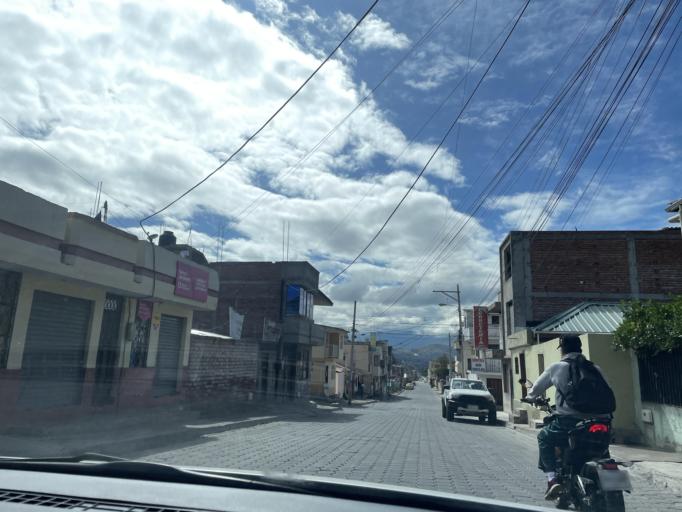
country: EC
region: Chimborazo
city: Guano
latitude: -1.6069
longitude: -78.6376
